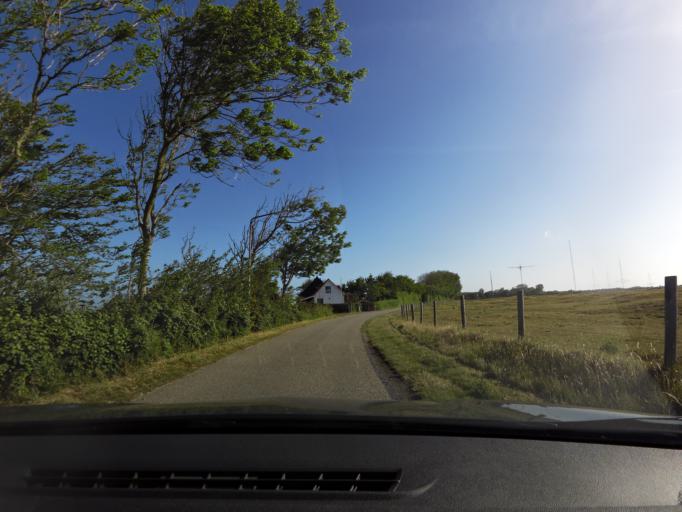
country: NL
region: South Holland
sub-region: Gemeente Goeree-Overflakkee
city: Ouddorp
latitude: 51.8057
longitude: 3.8859
